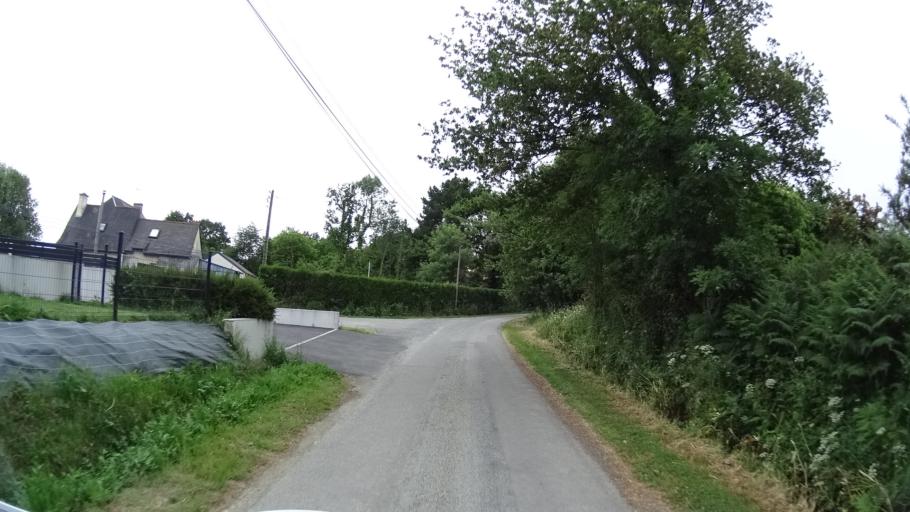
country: FR
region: Brittany
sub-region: Departement d'Ille-et-Vilaine
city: Crevin
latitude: 47.9630
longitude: -1.6802
